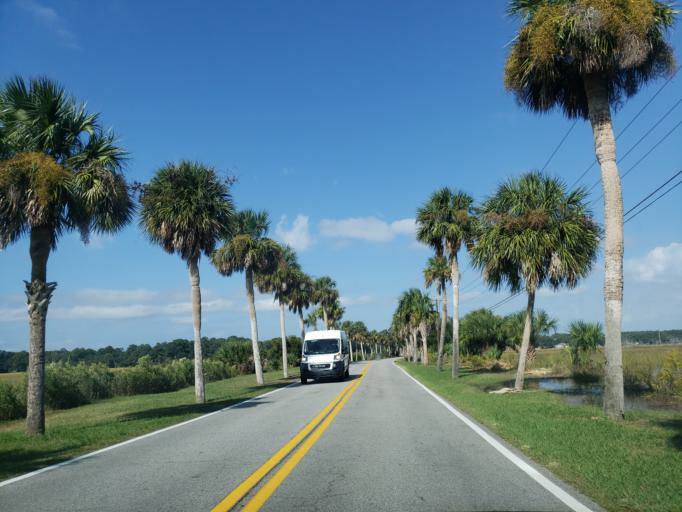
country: US
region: Georgia
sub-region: Chatham County
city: Montgomery
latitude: 31.9331
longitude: -81.0985
